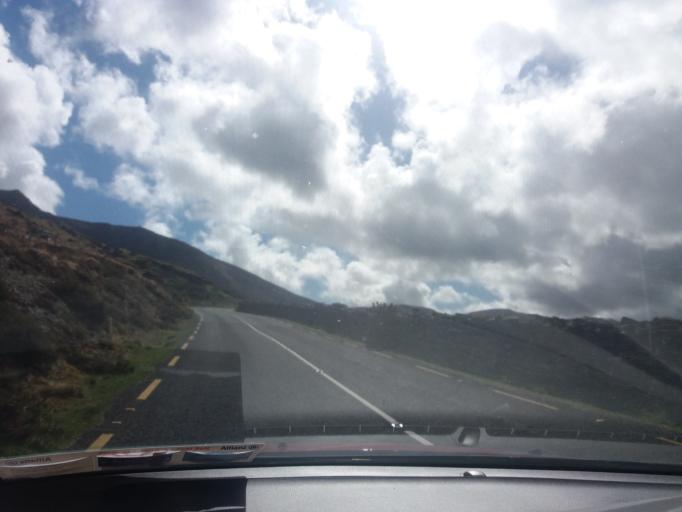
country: IE
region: Munster
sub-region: Ciarrai
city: Dingle
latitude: 52.2022
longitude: -10.1767
